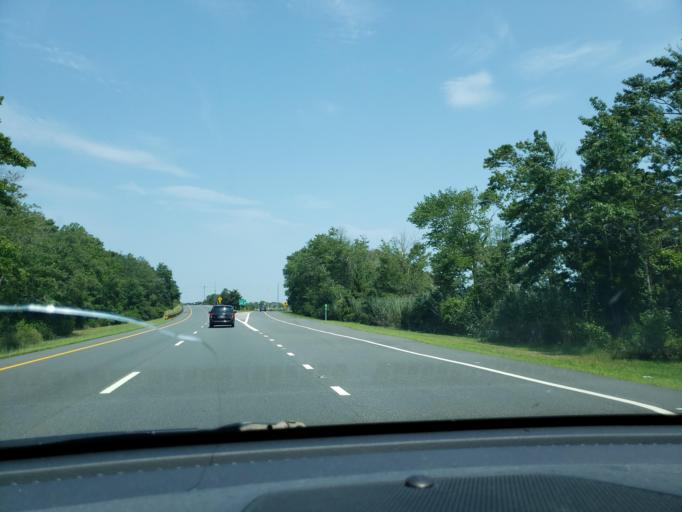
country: US
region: New Jersey
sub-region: Cape May County
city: Ocean City
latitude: 39.2585
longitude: -74.6450
